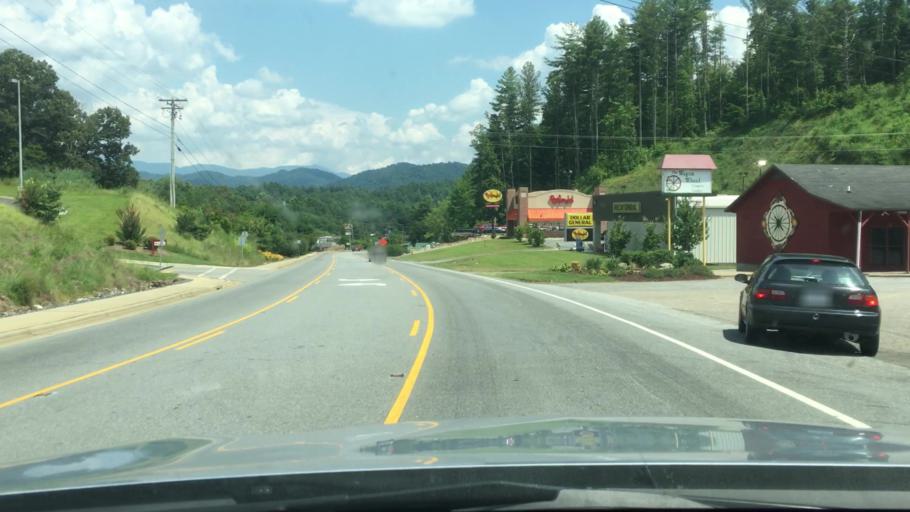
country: US
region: North Carolina
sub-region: Madison County
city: Mars Hill
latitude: 35.8229
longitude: -82.5440
